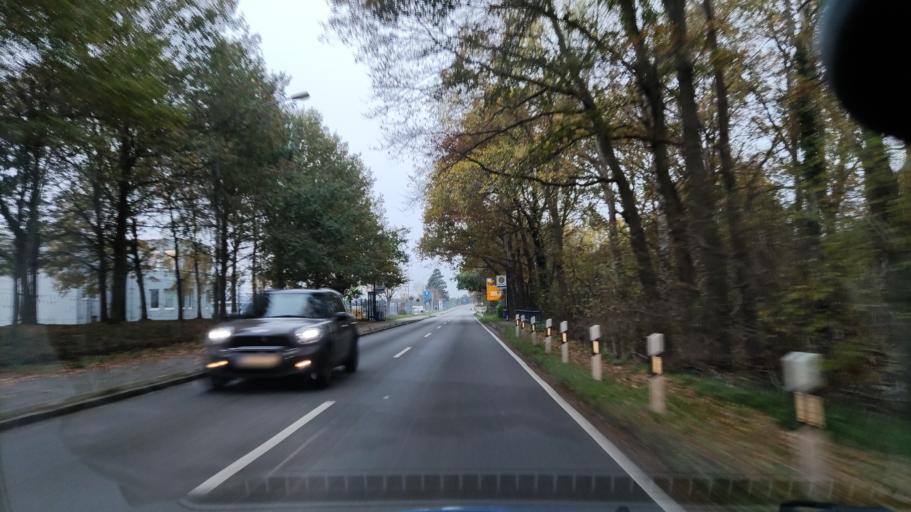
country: DE
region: Schleswig-Holstein
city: Gross Gronau
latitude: 53.8071
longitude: 10.7031
